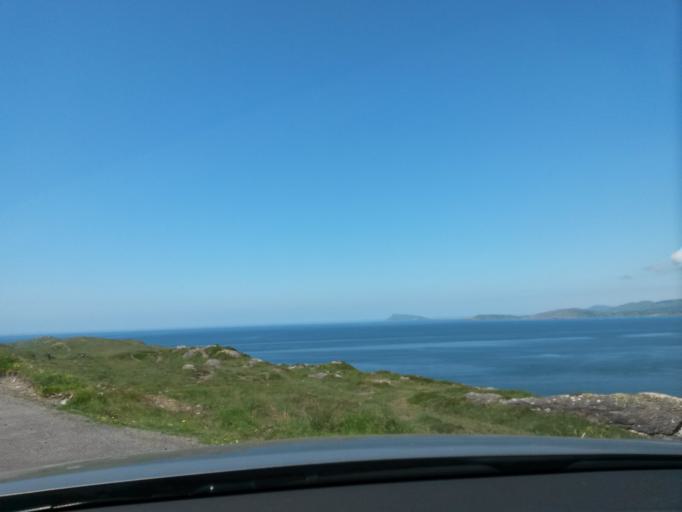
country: IE
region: Munster
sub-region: Ciarrai
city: Cahersiveen
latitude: 51.7252
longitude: -9.9851
